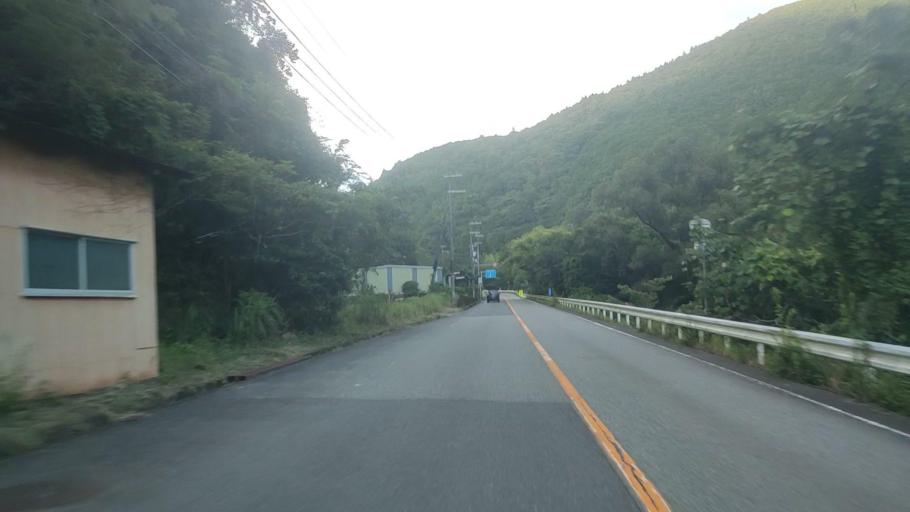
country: JP
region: Wakayama
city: Tanabe
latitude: 33.8141
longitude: 135.5515
